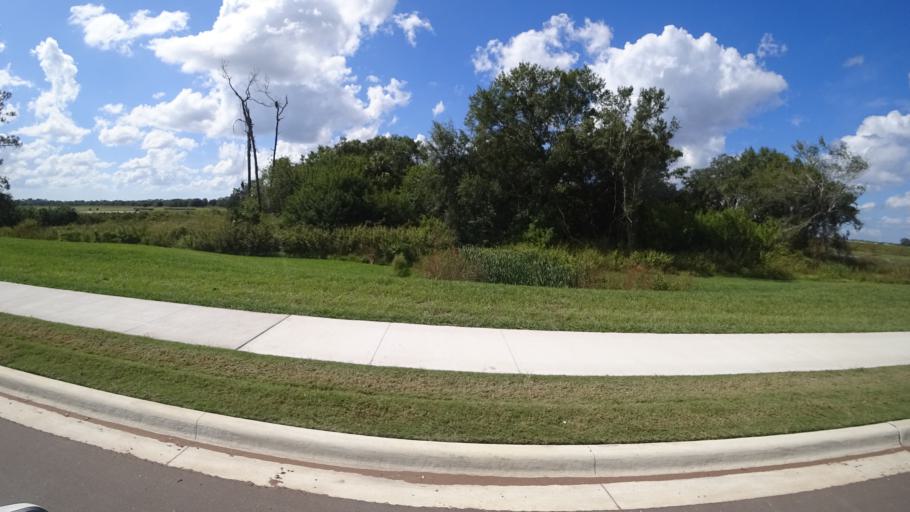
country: US
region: Florida
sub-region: Sarasota County
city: The Meadows
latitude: 27.4435
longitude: -82.3713
